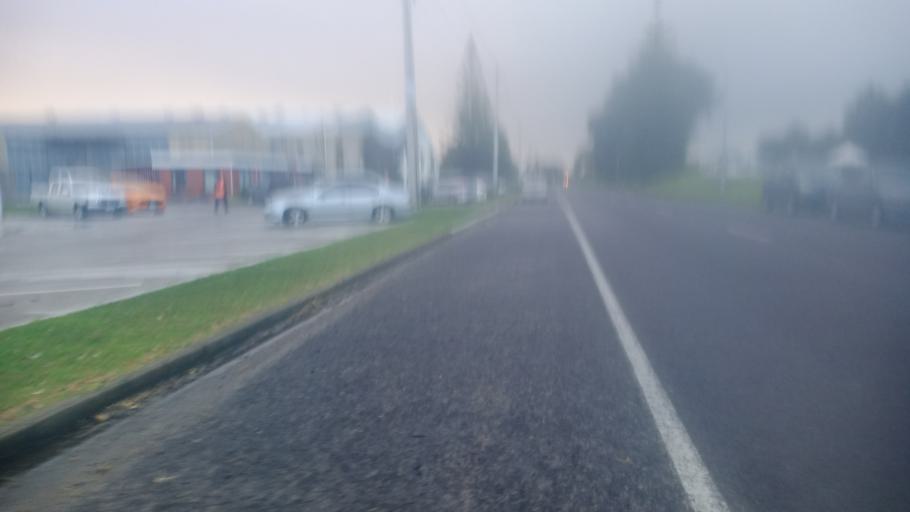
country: NZ
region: Gisborne
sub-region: Gisborne District
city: Gisborne
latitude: -38.6671
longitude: 177.9944
